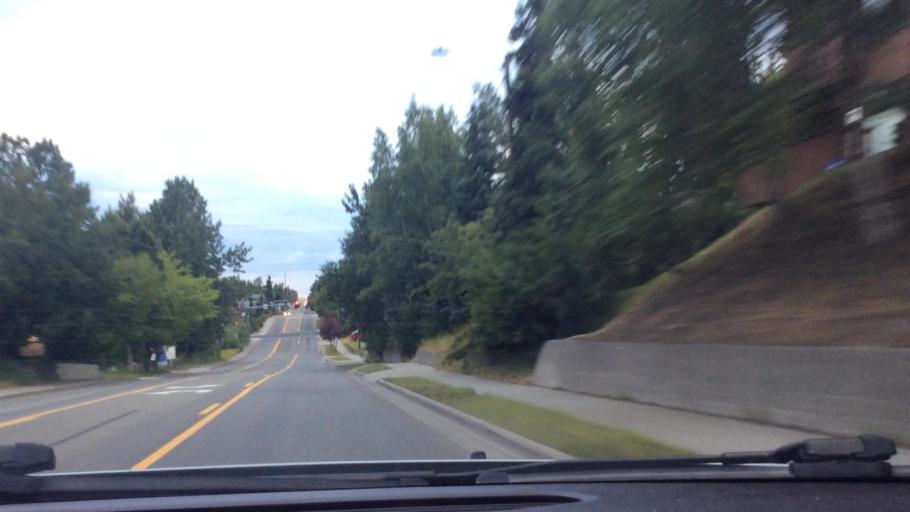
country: US
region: Alaska
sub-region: Anchorage Municipality
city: Anchorage
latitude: 61.2077
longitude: -149.8838
